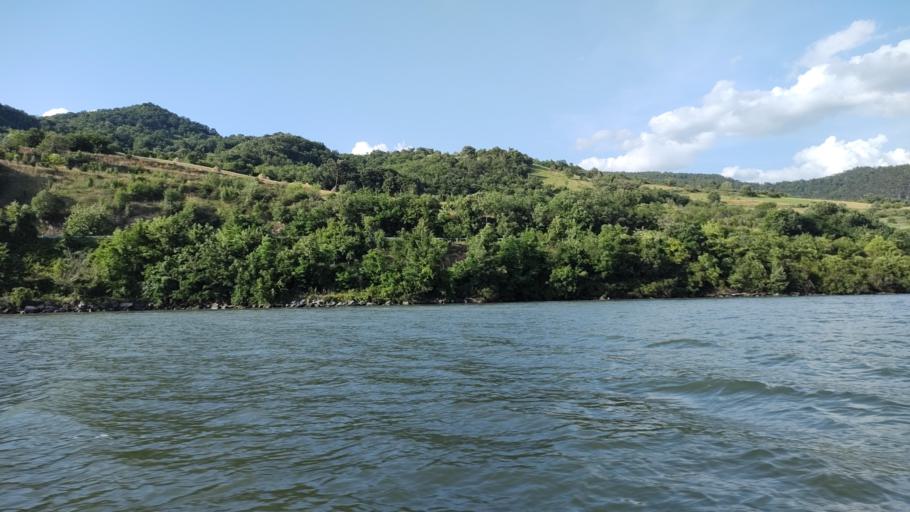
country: RO
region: Mehedinti
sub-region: Comuna Svinita
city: Svinita
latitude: 44.4800
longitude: 22.1285
